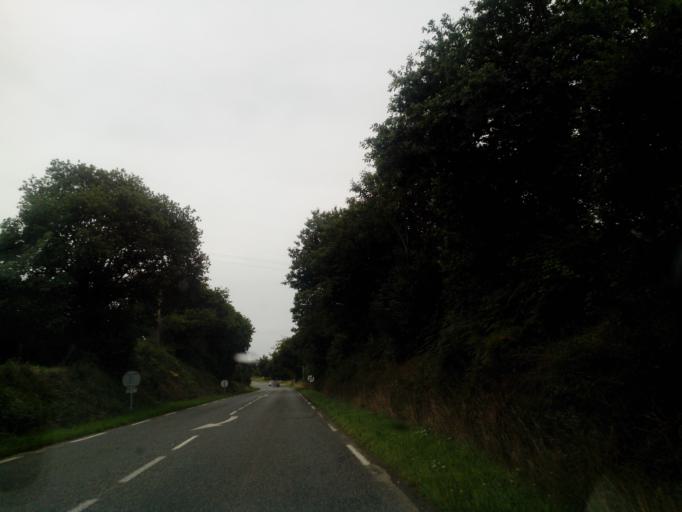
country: FR
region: Brittany
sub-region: Departement du Finistere
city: Quimperle
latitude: 47.8544
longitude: -3.5127
